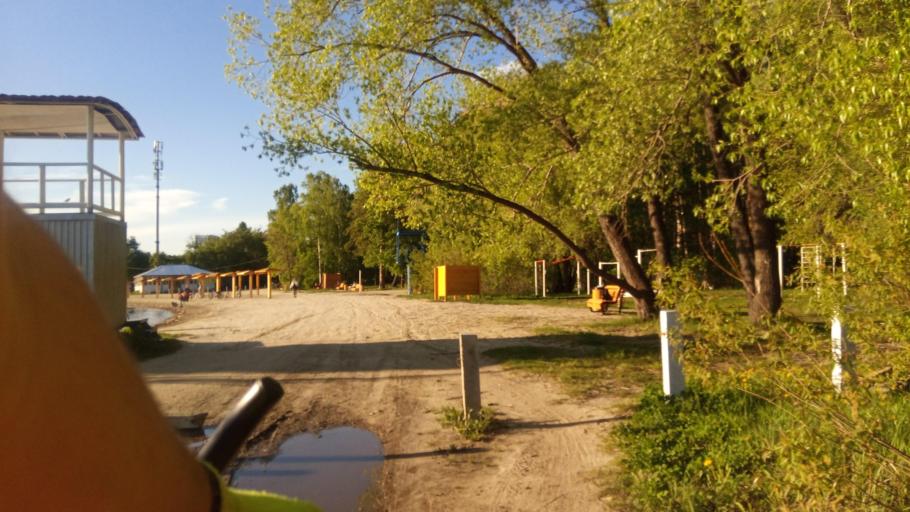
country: RU
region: Chelyabinsk
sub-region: Gorod Chelyabinsk
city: Chelyabinsk
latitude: 55.1446
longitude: 61.3295
